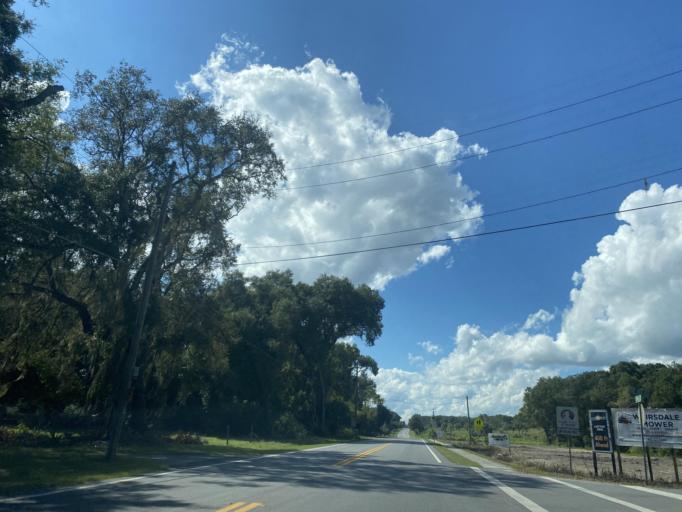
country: US
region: Florida
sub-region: Sumter County
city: The Villages
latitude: 28.9820
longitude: -81.9279
